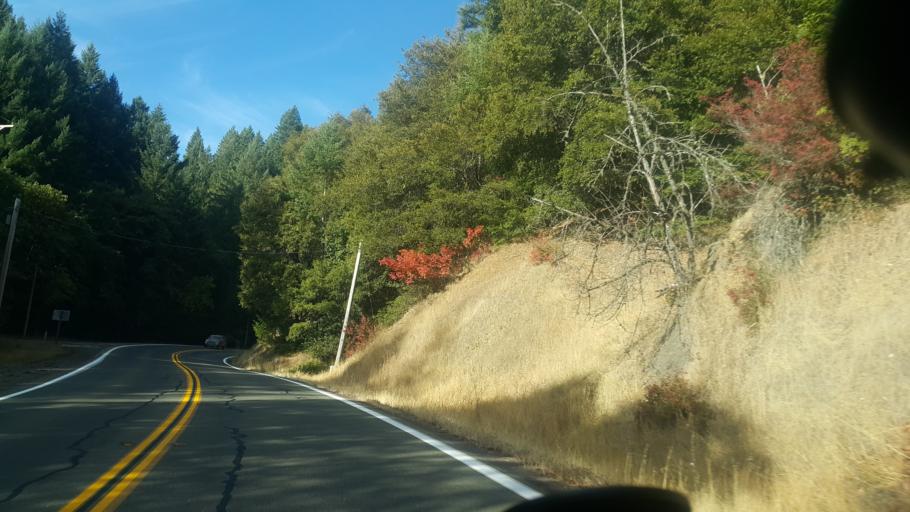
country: US
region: California
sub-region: Mendocino County
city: Brooktrails
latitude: 39.3880
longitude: -123.4347
